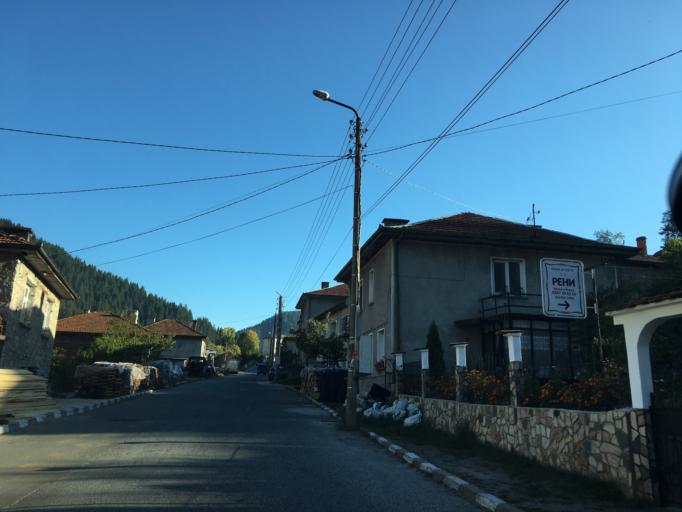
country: BG
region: Smolyan
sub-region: Obshtina Borino
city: Borino
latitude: 41.6019
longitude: 24.3788
